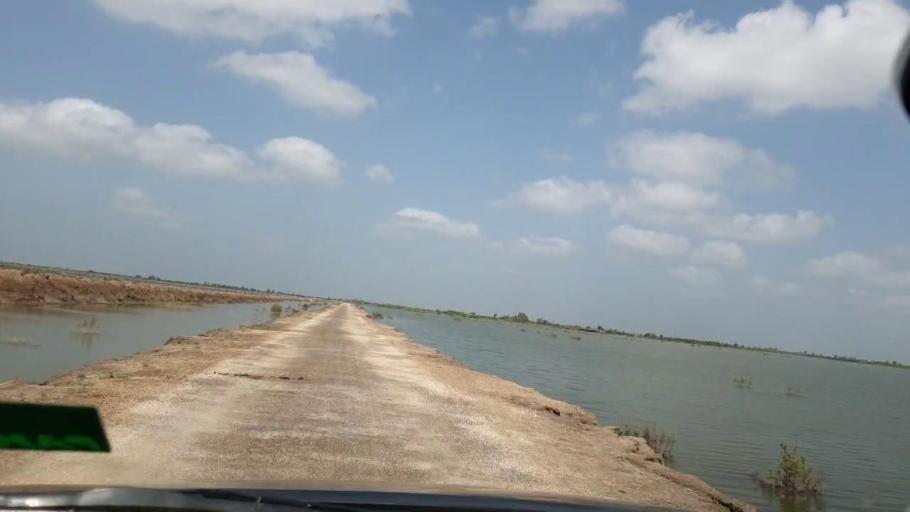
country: PK
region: Sindh
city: Kadhan
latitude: 24.5883
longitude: 69.1381
